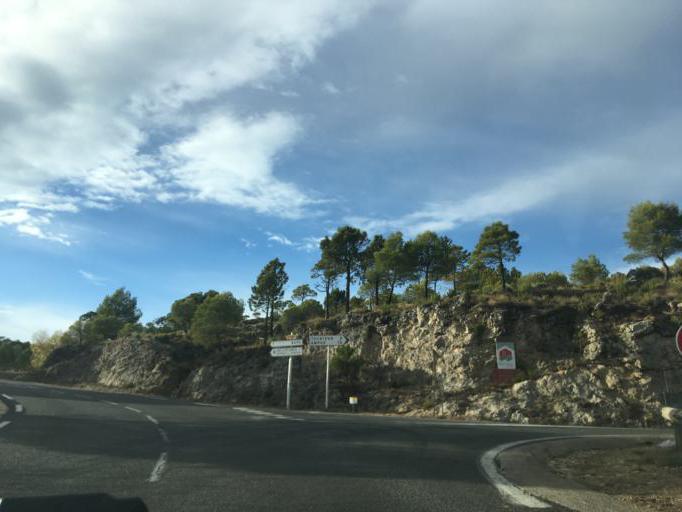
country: FR
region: Provence-Alpes-Cote d'Azur
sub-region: Departement du Var
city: Villecroze
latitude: 43.5848
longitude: 6.2686
